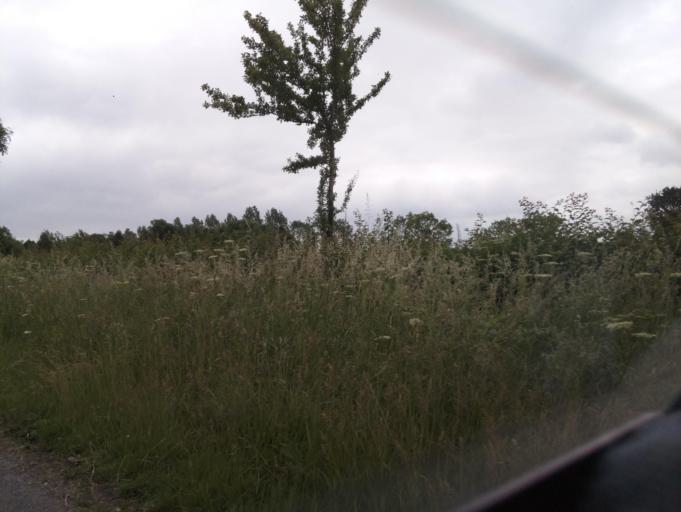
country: GB
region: England
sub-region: District of Rutland
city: Langham
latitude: 52.6726
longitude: -0.7804
